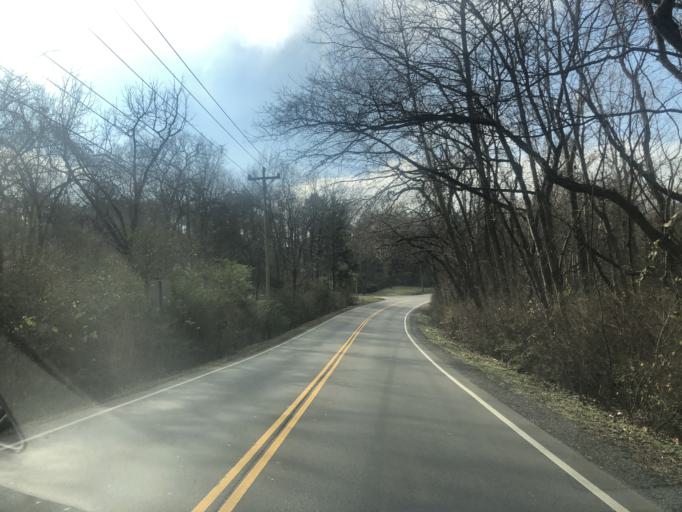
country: US
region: Tennessee
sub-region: Rutherford County
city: La Vergne
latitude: 36.0767
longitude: -86.6589
